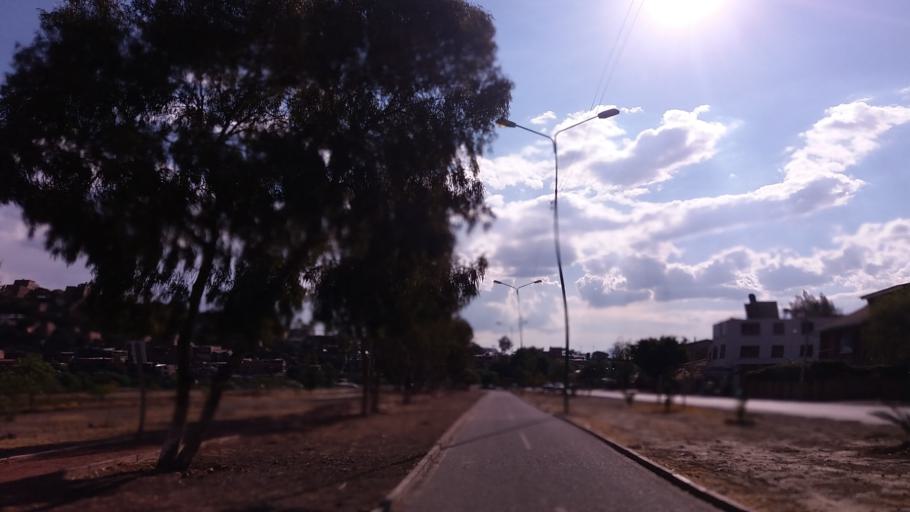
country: BO
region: Cochabamba
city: Cochabamba
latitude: -17.4010
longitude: -66.1441
